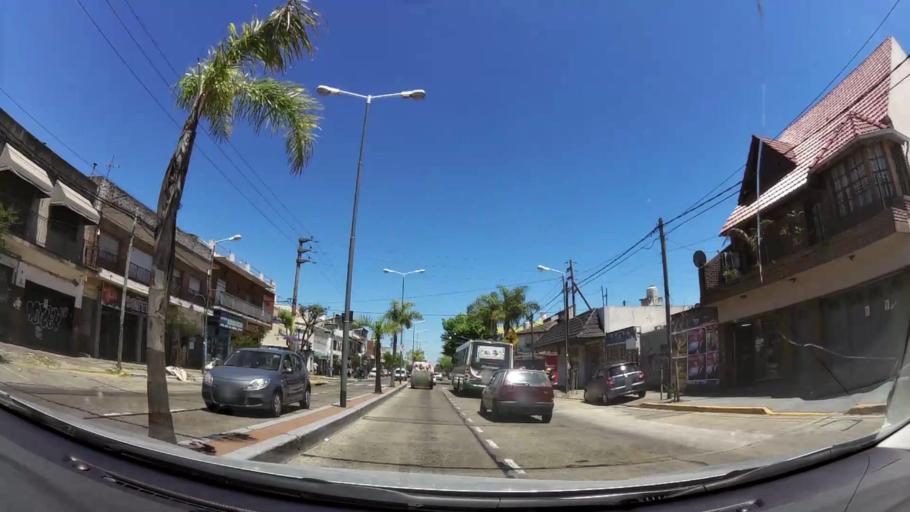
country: AR
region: Buenos Aires
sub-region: Partido de Tigre
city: Tigre
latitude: -34.4548
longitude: -58.5602
